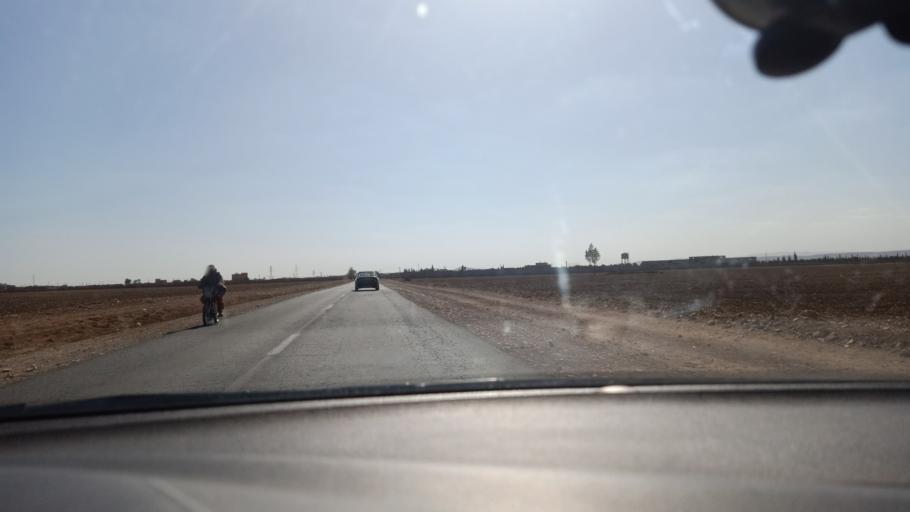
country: MA
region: Doukkala-Abda
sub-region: Safi
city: Youssoufia
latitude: 32.1221
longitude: -8.6033
